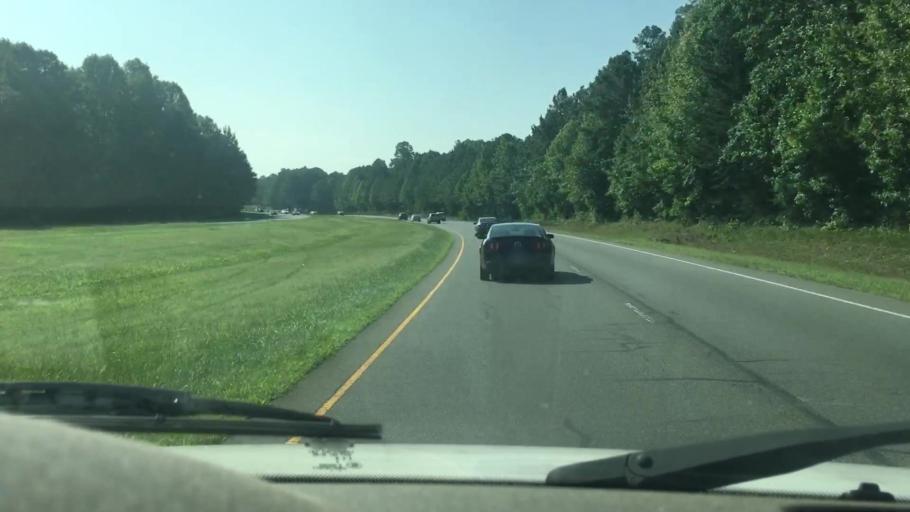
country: US
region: North Carolina
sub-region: Gaston County
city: Mount Holly
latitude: 35.3416
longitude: -80.9666
